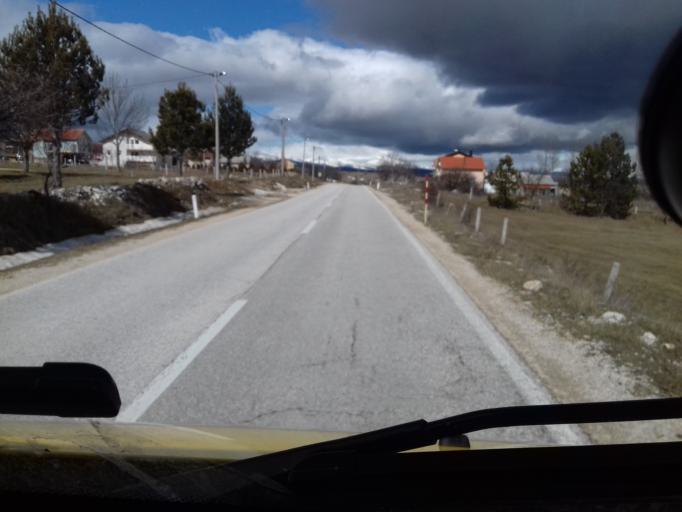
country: BA
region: Federation of Bosnia and Herzegovina
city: Dreznica
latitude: 43.6086
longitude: 17.2701
